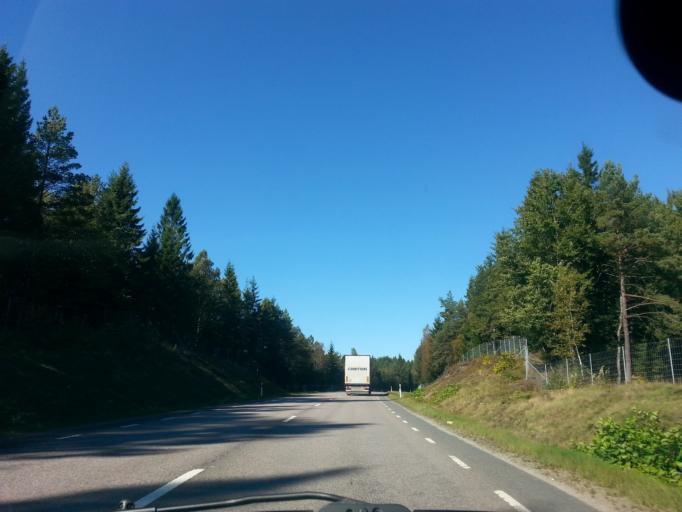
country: SE
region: Vaestra Goetaland
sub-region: Harryda Kommun
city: Hindas
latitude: 57.6565
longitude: 12.3753
